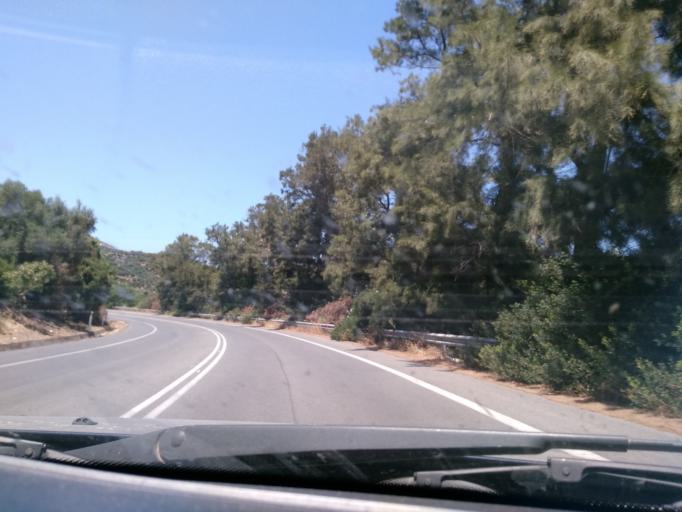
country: GR
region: Crete
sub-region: Nomos Rethymnis
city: Anogeia
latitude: 35.3981
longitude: 24.8783
